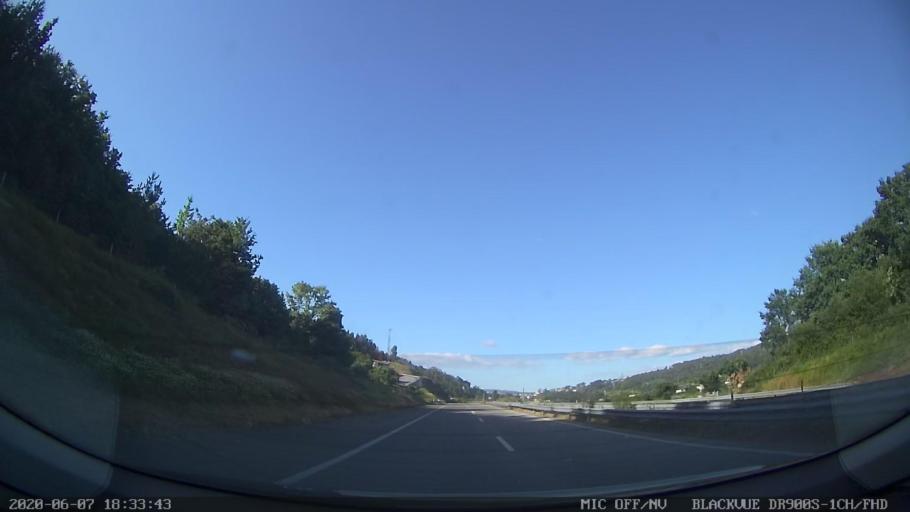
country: PT
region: Braga
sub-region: Guimaraes
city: Serzedo
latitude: 41.4195
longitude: -8.2002
